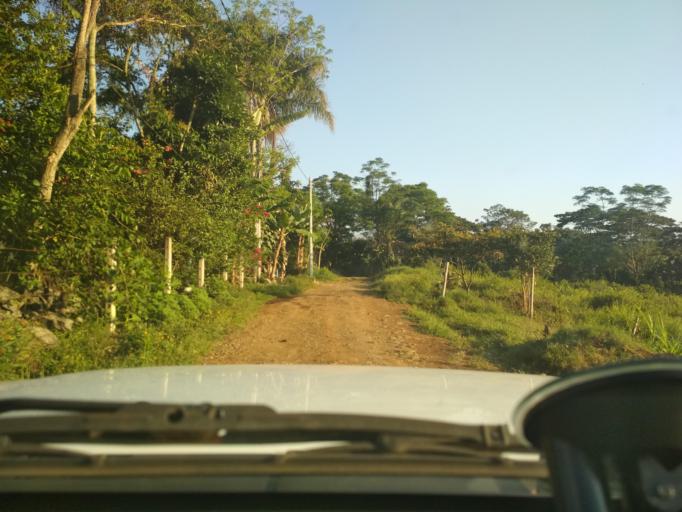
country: MX
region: Veracruz
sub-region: Fortin
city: Fraccionamiento Villas de la Llave
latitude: 18.9214
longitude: -97.0000
